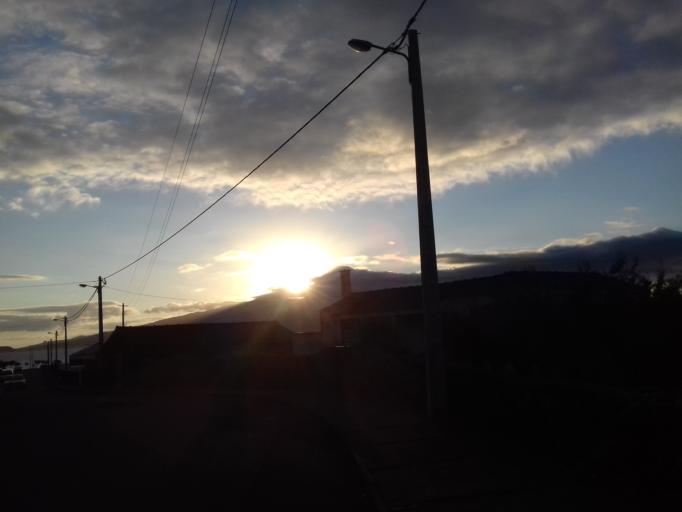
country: PT
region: Azores
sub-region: Madalena
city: Madalena
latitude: 38.5332
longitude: -28.5316
